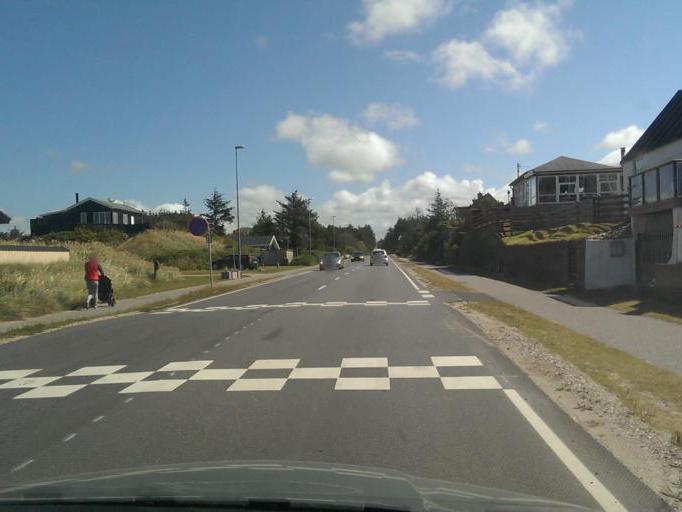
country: DK
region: North Denmark
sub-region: Jammerbugt Kommune
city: Pandrup
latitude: 57.2509
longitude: 9.5925
